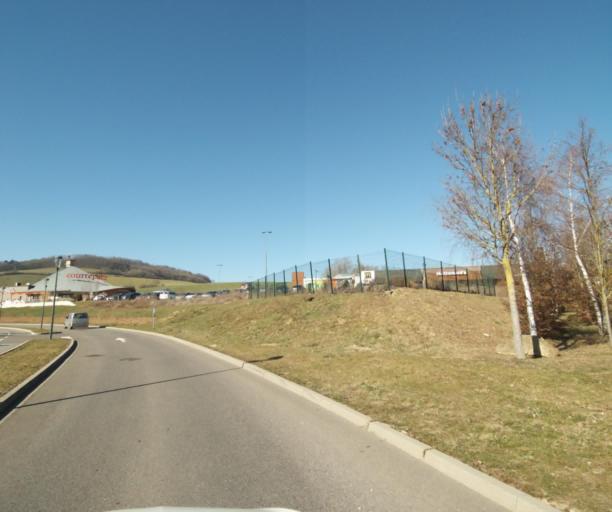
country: FR
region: Lorraine
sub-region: Departement de Meurthe-et-Moselle
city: Pulnoy
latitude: 48.7110
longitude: 6.2425
